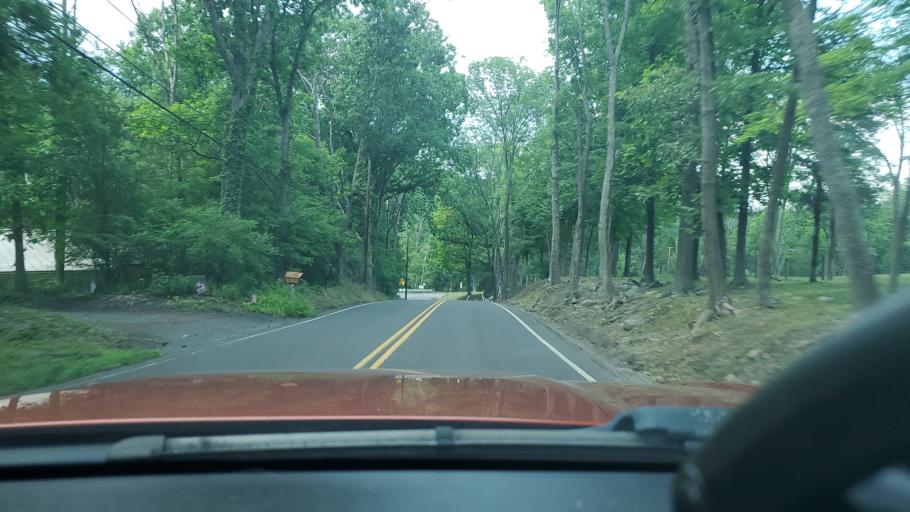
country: US
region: Pennsylvania
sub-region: Montgomery County
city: Limerick
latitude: 40.2708
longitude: -75.5148
